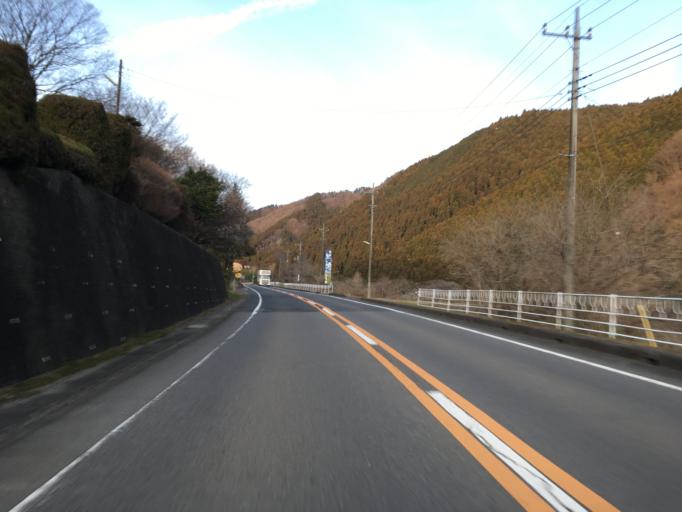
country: JP
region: Ibaraki
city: Daigo
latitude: 36.8343
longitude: 140.3816
